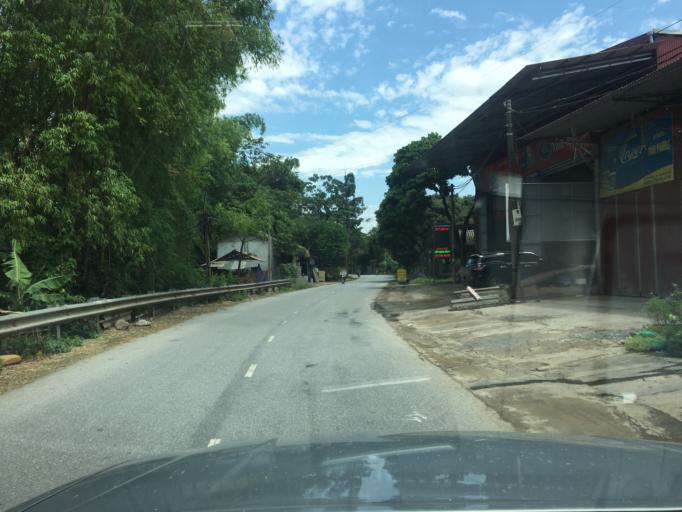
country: VN
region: Yen Bai
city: Son Thinh
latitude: 21.6534
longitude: 104.5009
